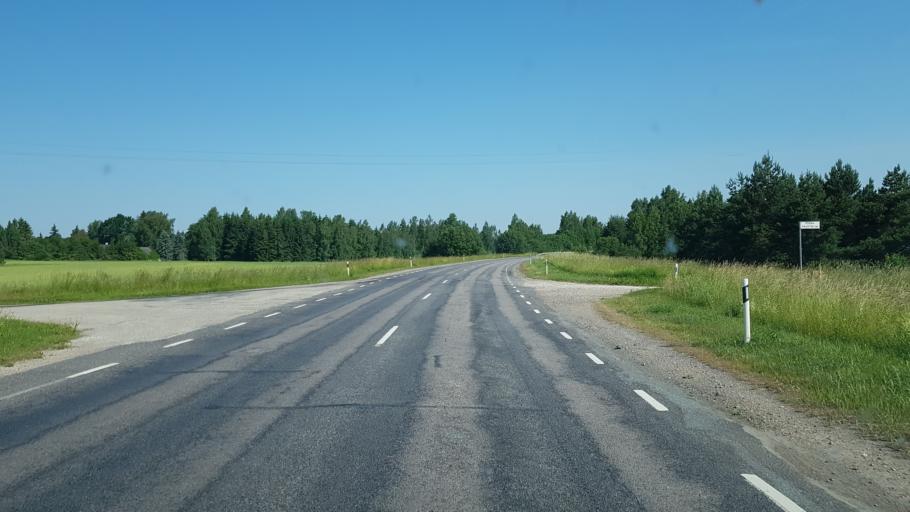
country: EE
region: Tartu
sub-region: UElenurme vald
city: Ulenurme
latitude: 58.2796
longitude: 26.7293
